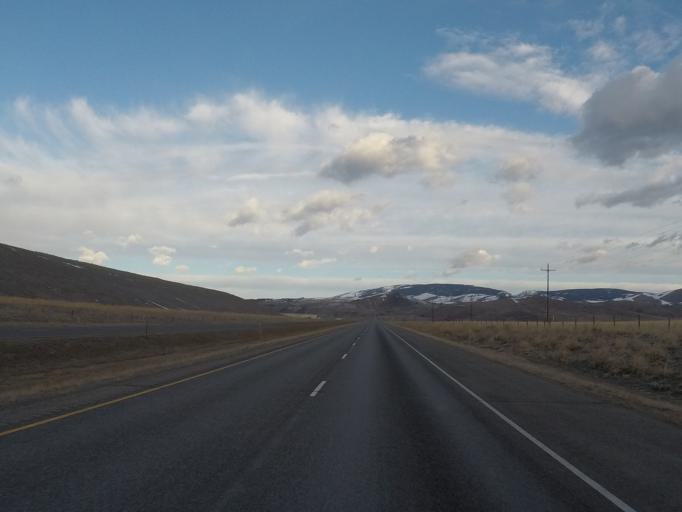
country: US
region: Montana
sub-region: Deer Lodge County
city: Anaconda
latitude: 46.1240
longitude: -112.8870
